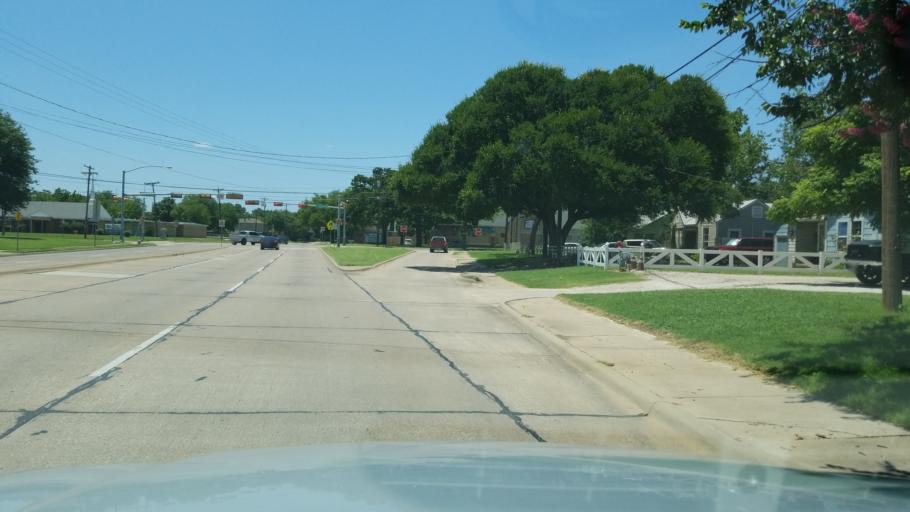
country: US
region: Texas
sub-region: Dallas County
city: Irving
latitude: 32.8013
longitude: -96.9246
